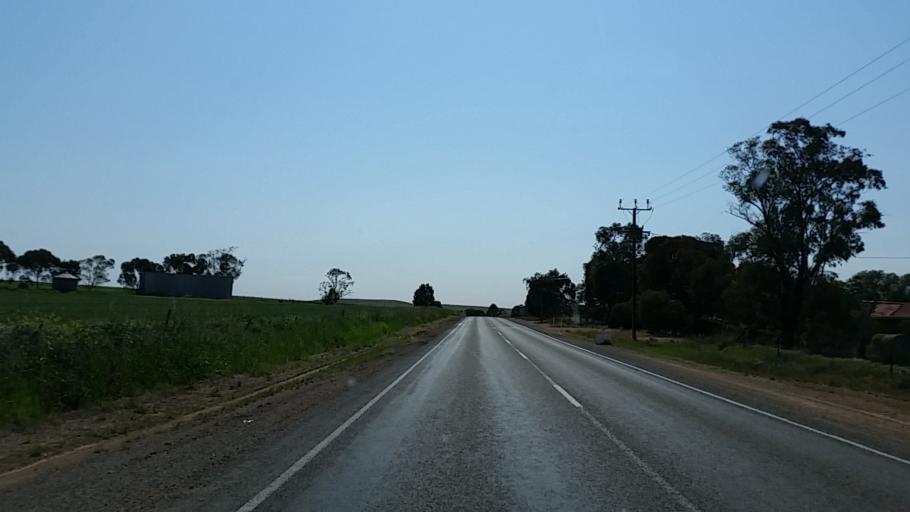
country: AU
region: South Australia
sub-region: Port Pirie City and Dists
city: Crystal Brook
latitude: -33.2567
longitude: 138.3592
